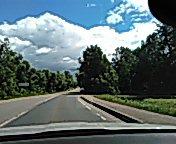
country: RU
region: Moskovskaya
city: Shevlyakovo
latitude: 56.4989
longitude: 36.8562
